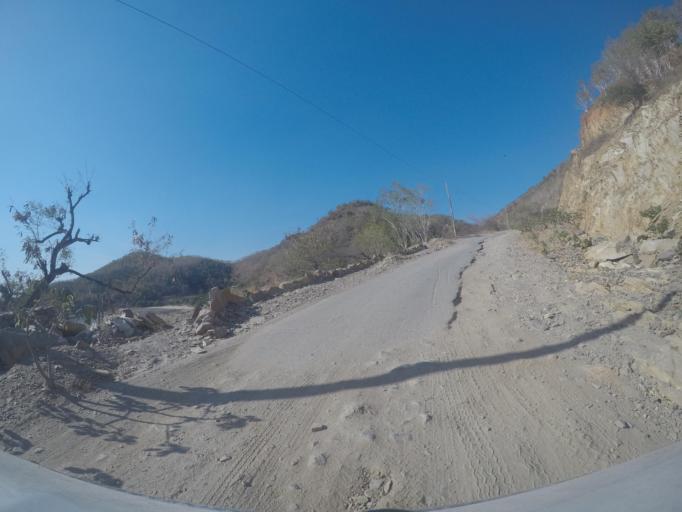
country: TL
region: Dili
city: Dili
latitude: -8.5348
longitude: 125.6153
